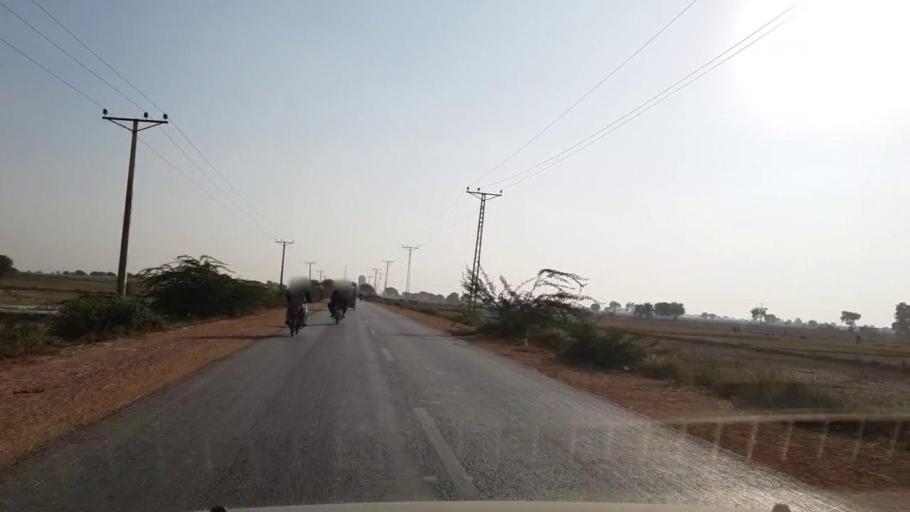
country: PK
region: Sindh
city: Bulri
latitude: 24.8405
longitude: 68.3249
